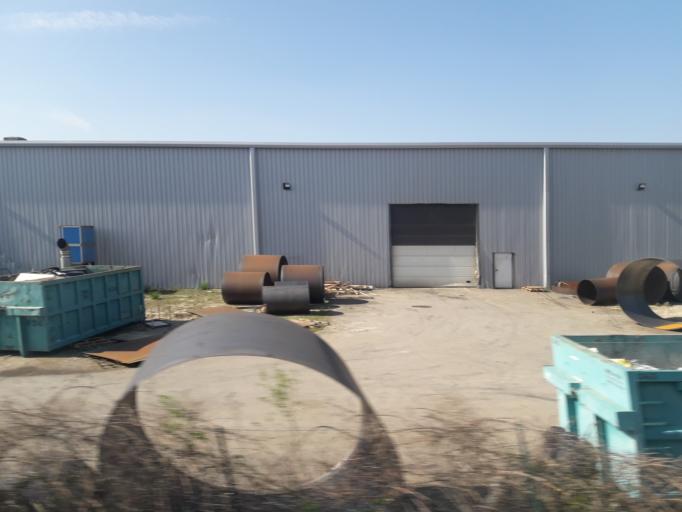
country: FR
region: Rhone-Alpes
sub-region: Departement de la Drome
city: Genissieux
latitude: 45.0565
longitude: 5.0915
